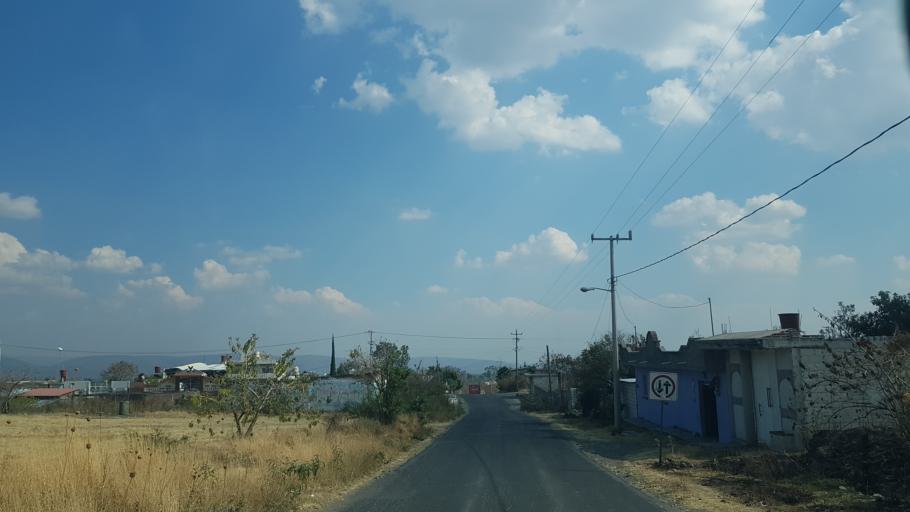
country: MX
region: Puebla
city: Atlixco
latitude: 18.9170
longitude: -98.4800
